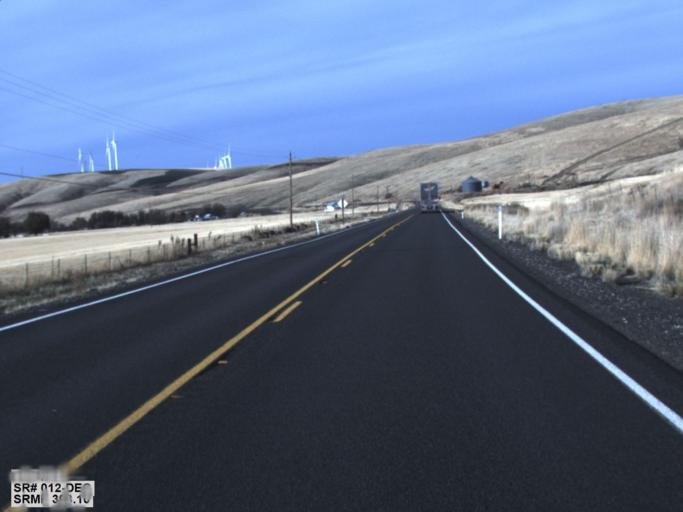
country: US
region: Washington
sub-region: Garfield County
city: Pomeroy
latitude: 46.5082
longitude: -117.7847
